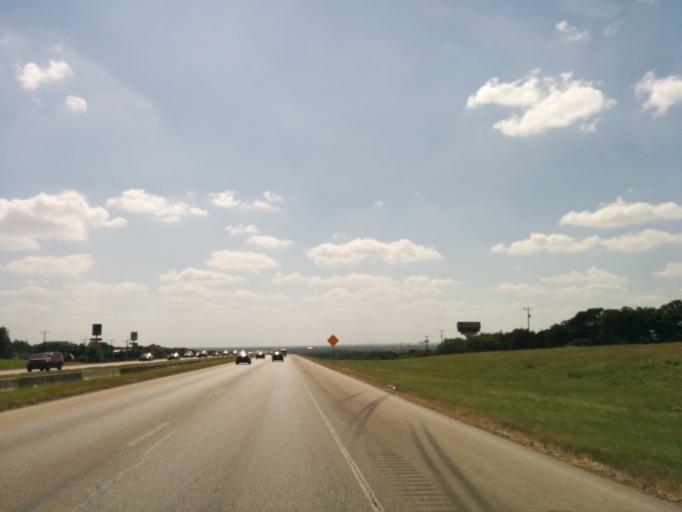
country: US
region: Texas
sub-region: Bexar County
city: Live Oak
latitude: 29.6026
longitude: -98.3835
